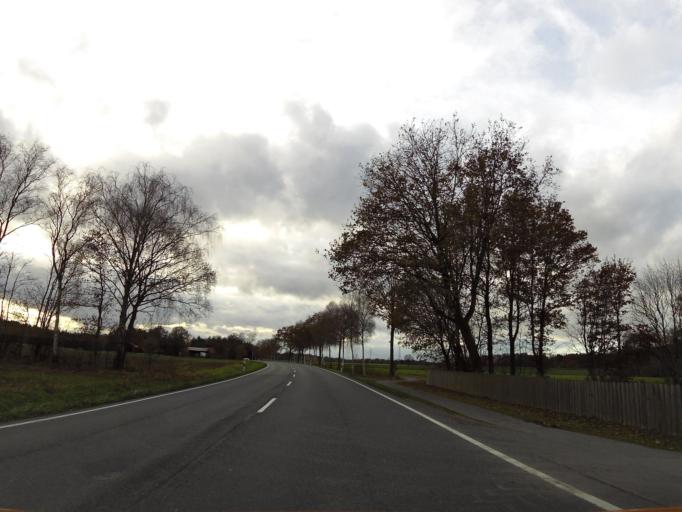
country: DE
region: Lower Saxony
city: Bispingen
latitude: 53.0164
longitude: 9.9937
